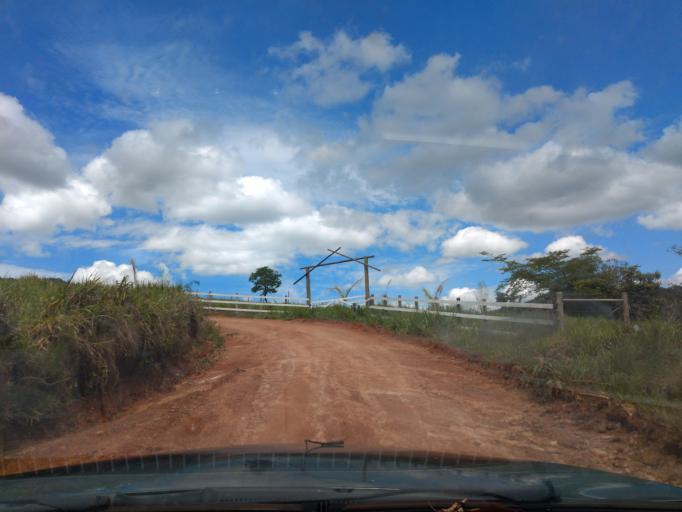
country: BR
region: Minas Gerais
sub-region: Lavras
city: Lavras
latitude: -21.5224
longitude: -44.9306
